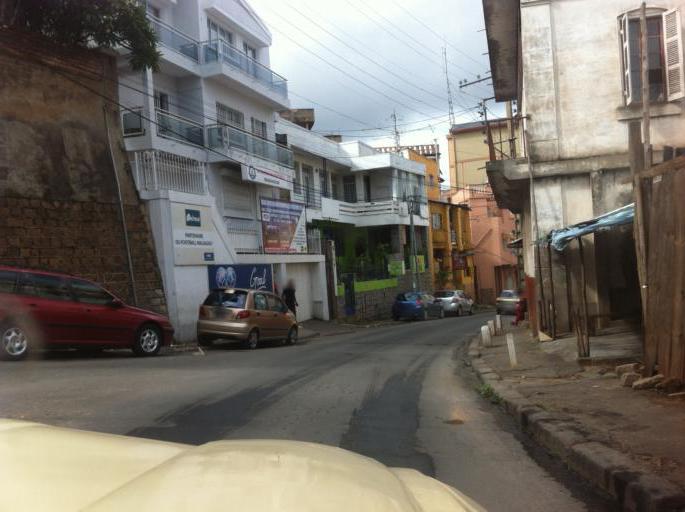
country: MG
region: Analamanga
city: Antananarivo
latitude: -18.9119
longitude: 47.5205
